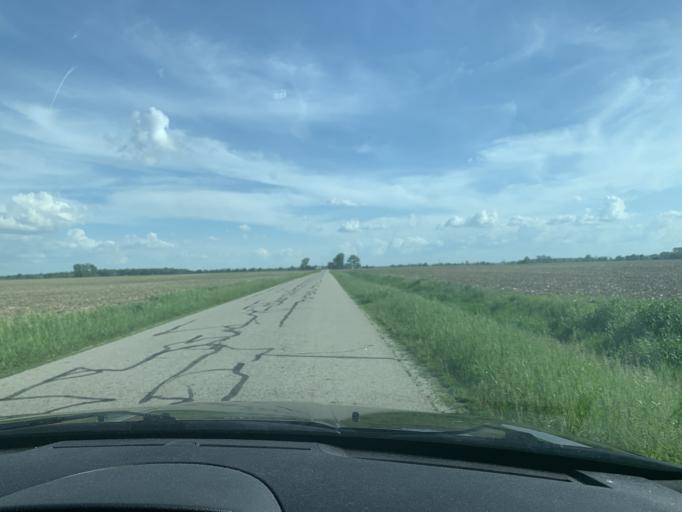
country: US
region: Ohio
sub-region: Logan County
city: De Graff
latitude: 40.2785
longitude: -84.0143
